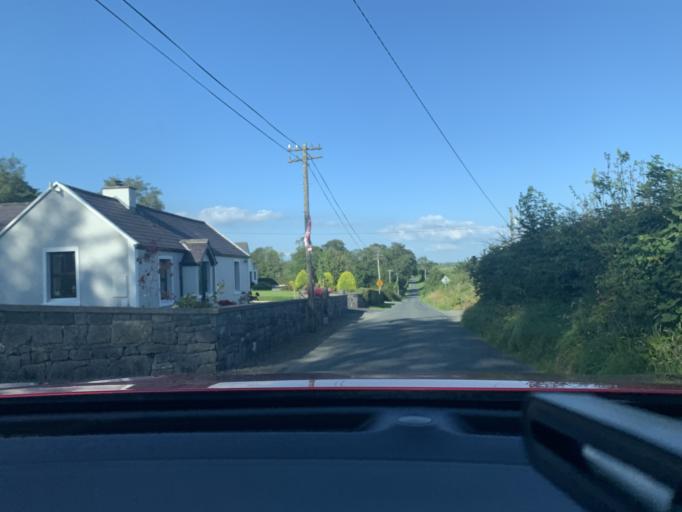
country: IE
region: Connaught
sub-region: Sligo
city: Tobercurry
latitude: 54.1371
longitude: -8.6976
